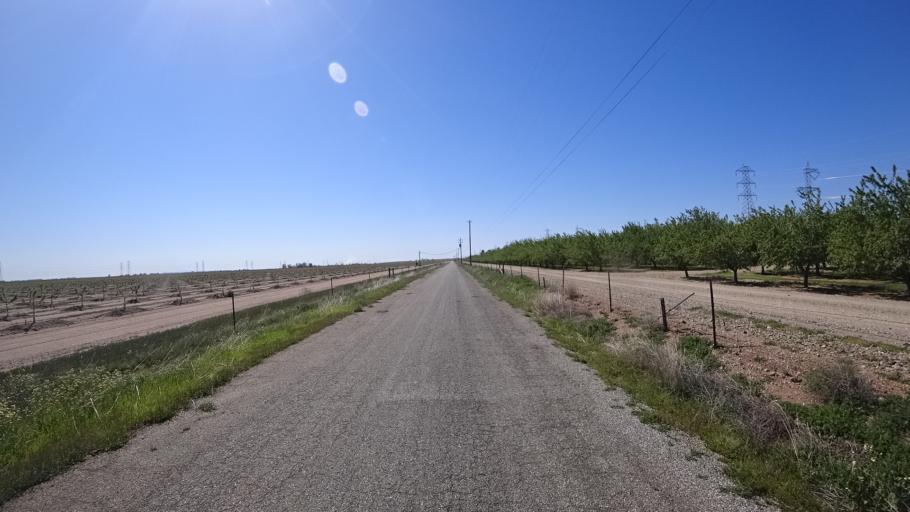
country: US
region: California
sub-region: Glenn County
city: Orland
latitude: 39.6630
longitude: -122.2719
